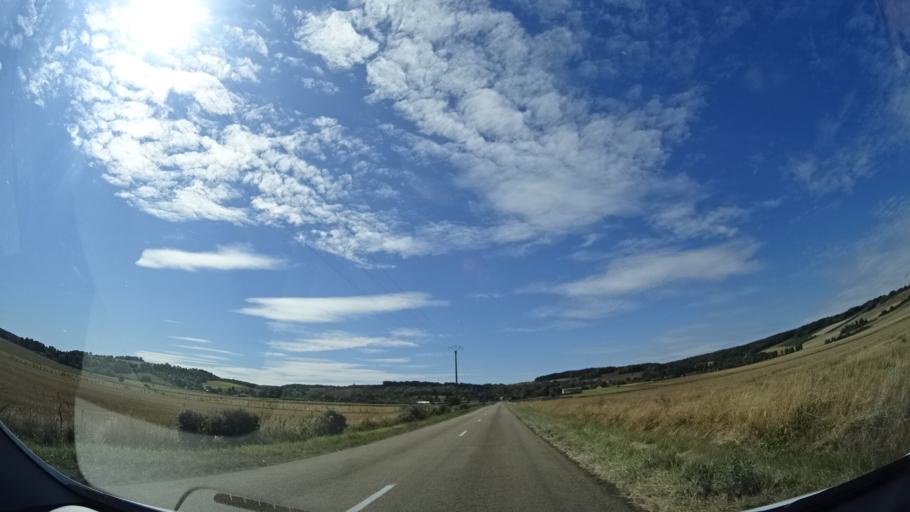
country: FR
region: Bourgogne
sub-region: Departement de l'Yonne
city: Aillant-sur-Tholon
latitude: 47.9155
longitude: 3.3395
